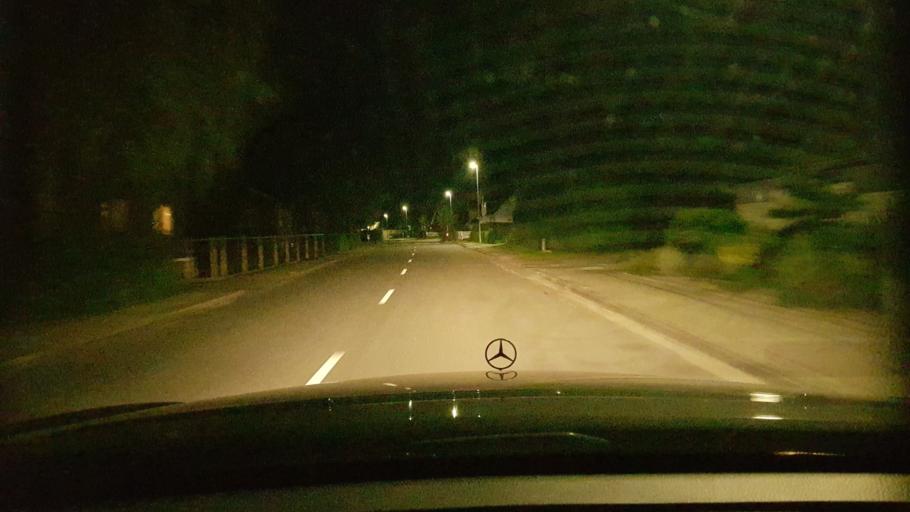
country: DK
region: North Denmark
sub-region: Mariagerfjord Kommune
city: Hadsund
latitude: 56.8043
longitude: 10.2670
